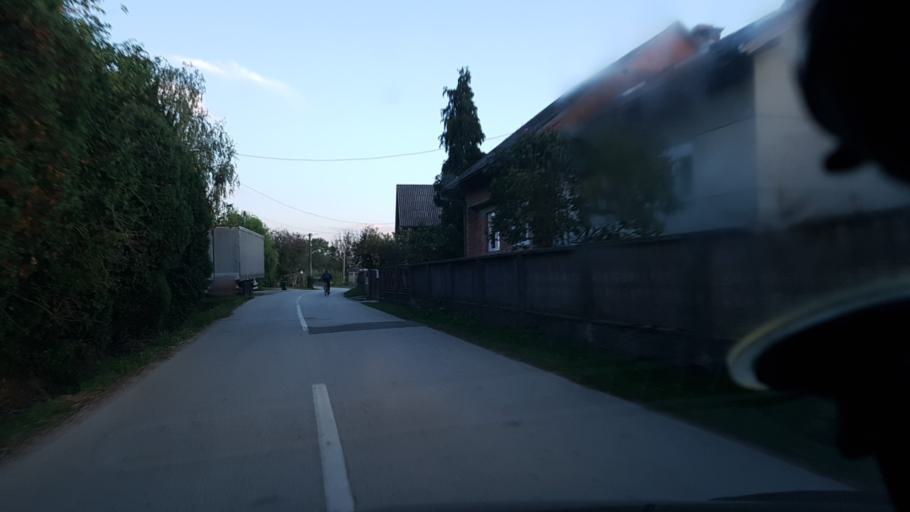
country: HR
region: Zagrebacka
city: Bregana
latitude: 45.8705
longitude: 15.7080
